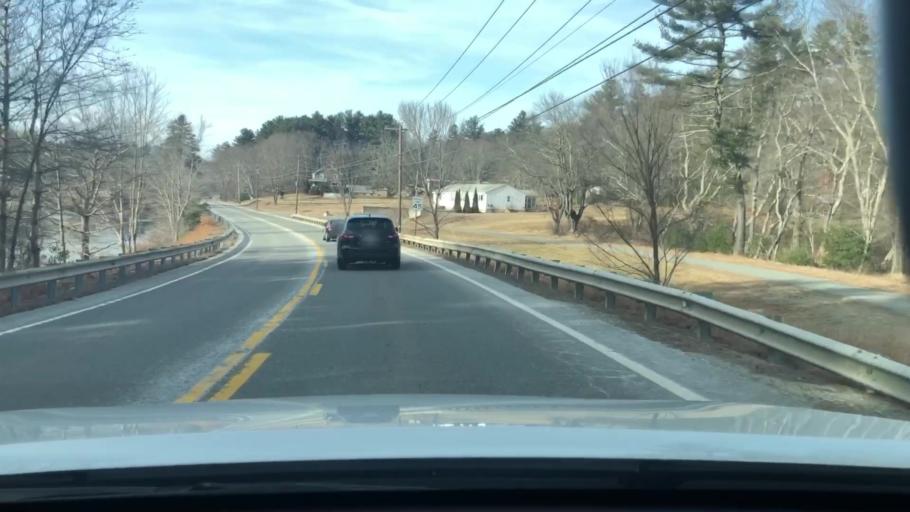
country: US
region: Massachusetts
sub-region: Worcester County
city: Northbridge
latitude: 42.1797
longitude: -71.6400
